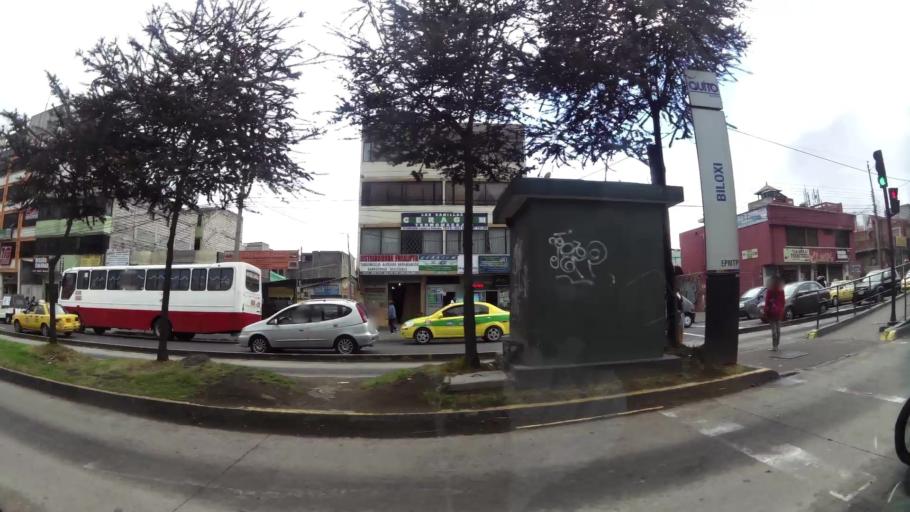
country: EC
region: Pichincha
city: Quito
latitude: -0.2572
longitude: -78.5434
